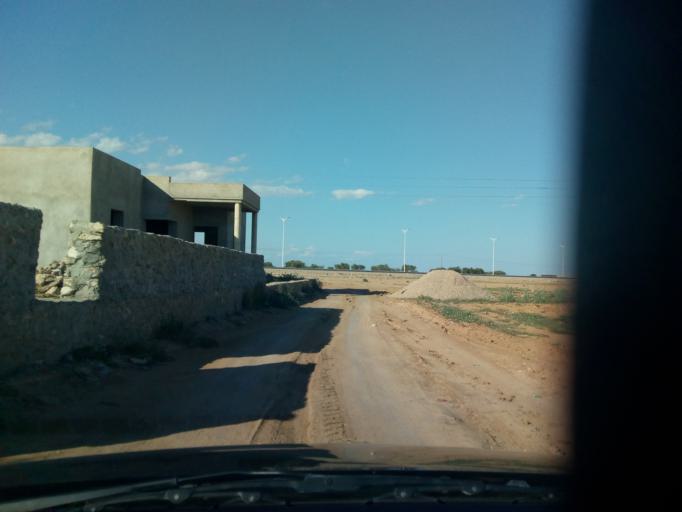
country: TN
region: Safaqis
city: Sfax
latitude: 34.7281
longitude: 10.6282
